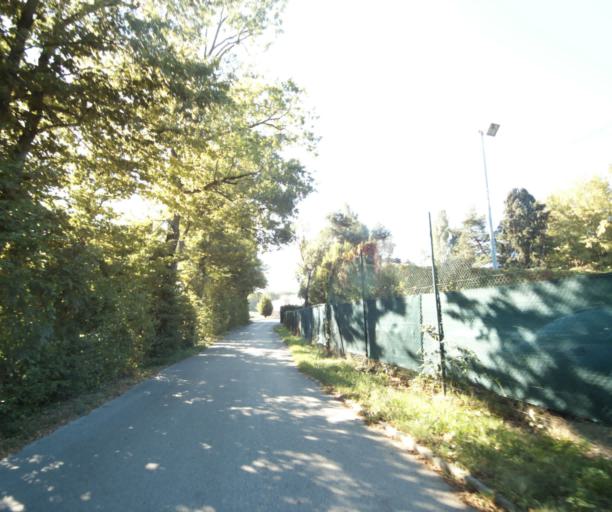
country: FR
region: Rhone-Alpes
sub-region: Departement de l'Ain
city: Ferney-Voltaire
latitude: 46.2469
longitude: 6.0952
